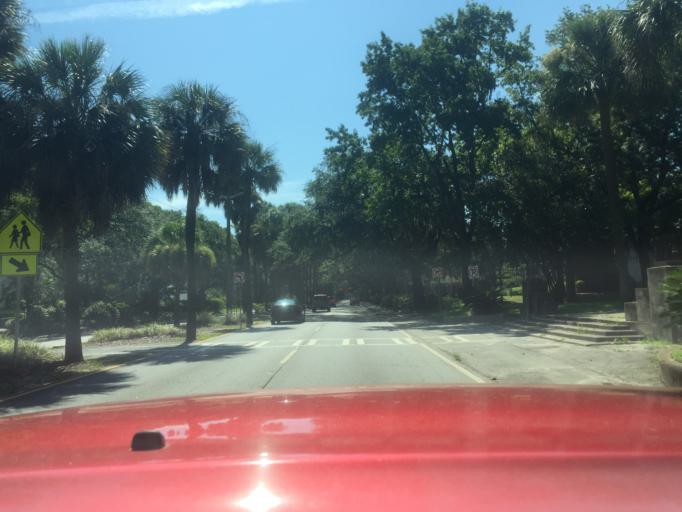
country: US
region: Georgia
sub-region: Chatham County
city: Savannah
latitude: 32.0499
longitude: -81.0919
